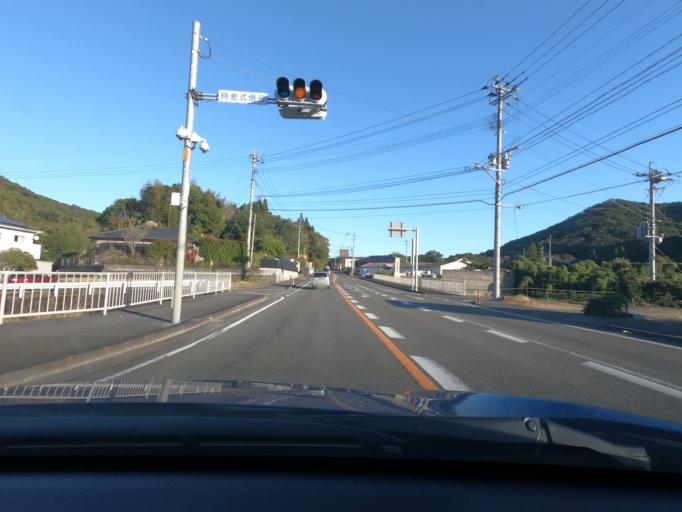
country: JP
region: Kagoshima
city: Satsumasendai
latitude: 31.8481
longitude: 130.2497
